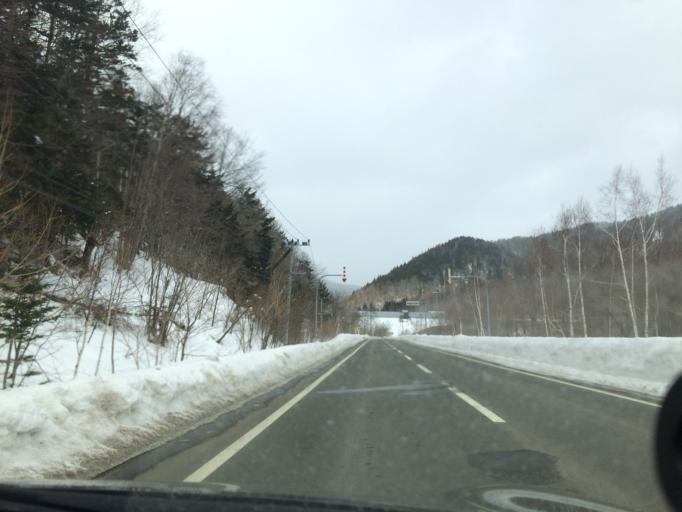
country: JP
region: Hokkaido
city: Shimo-furano
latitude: 43.0630
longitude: 142.5314
